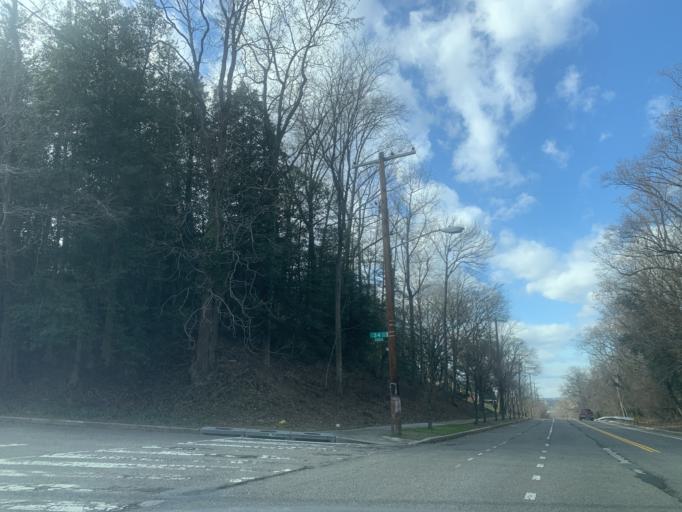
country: US
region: Maryland
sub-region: Prince George's County
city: Silver Hill
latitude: 38.8764
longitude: -76.9574
